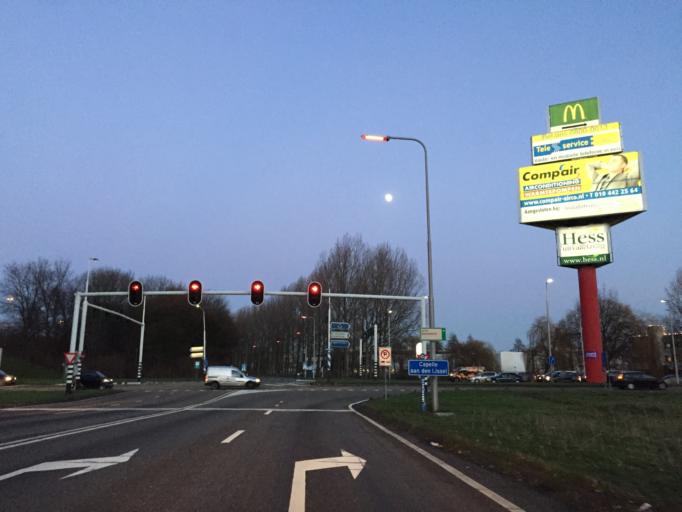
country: NL
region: South Holland
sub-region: Gemeente Capelle aan den IJssel
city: Capelle aan den IJssel
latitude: 51.9550
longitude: 4.5620
